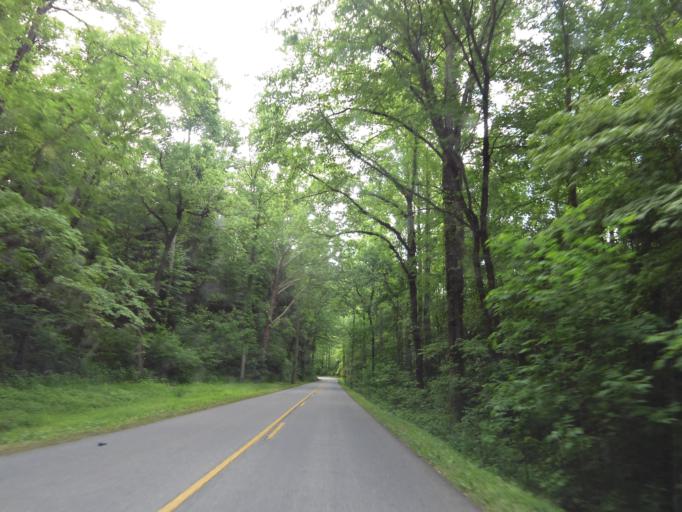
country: US
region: Tennessee
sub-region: Sevier County
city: Gatlinburg
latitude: 35.6797
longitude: -83.6500
